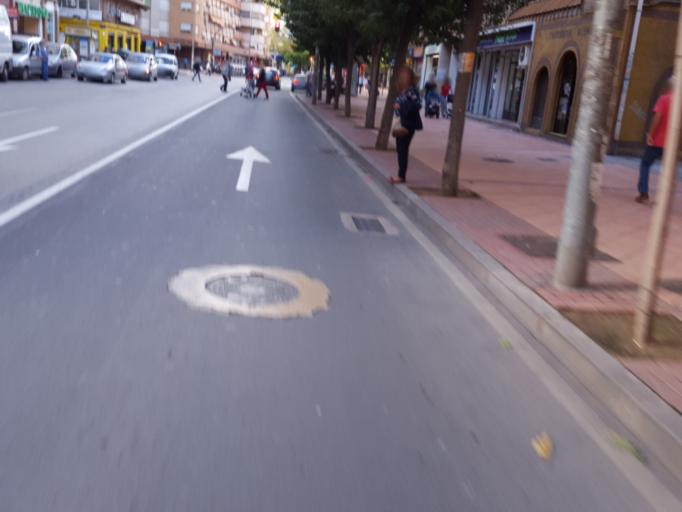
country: ES
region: Murcia
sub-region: Murcia
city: Murcia
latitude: 37.9907
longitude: -1.1405
